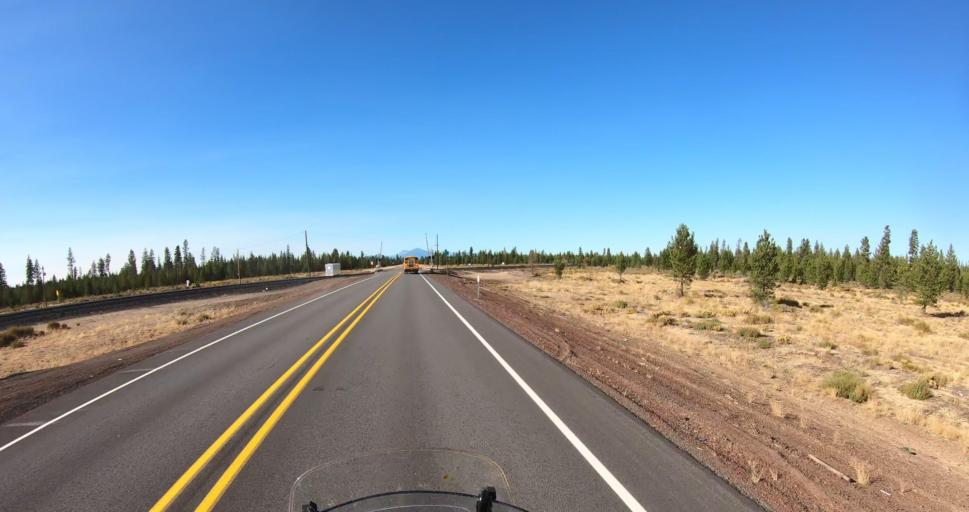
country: US
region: Oregon
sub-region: Deschutes County
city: La Pine
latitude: 43.6064
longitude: -121.5009
